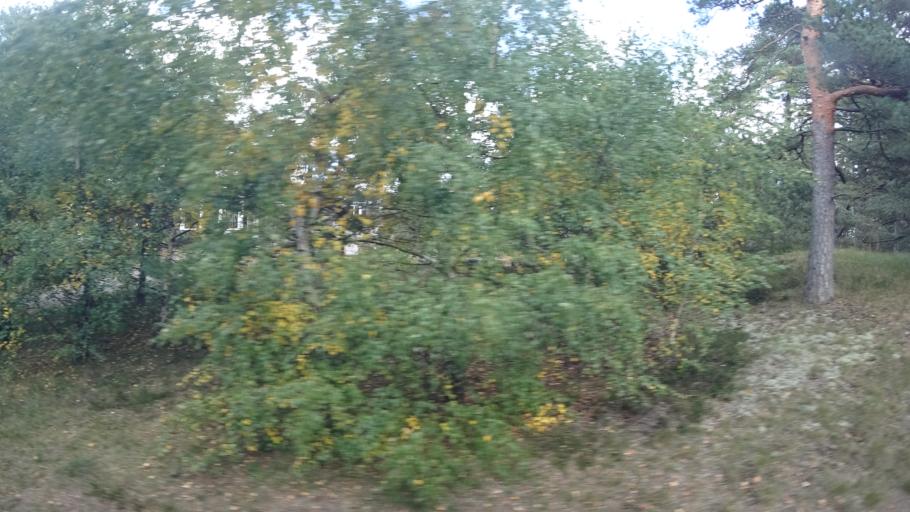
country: SE
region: Skane
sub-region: Kristianstads Kommun
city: Ahus
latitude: 55.9125
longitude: 14.2930
